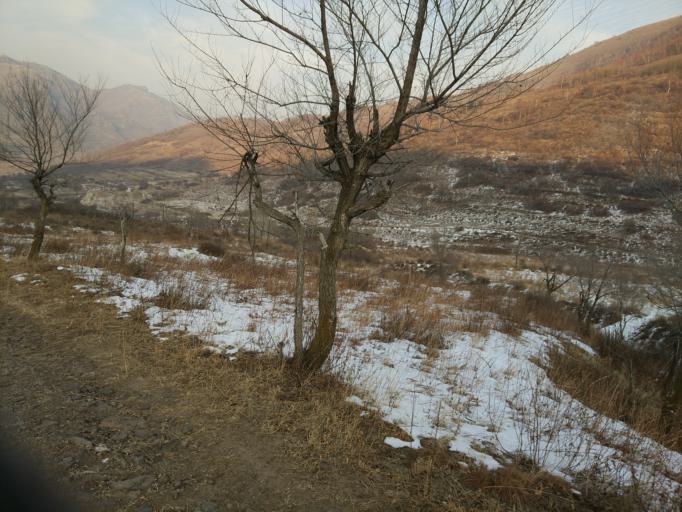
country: CN
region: Hebei
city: Xiwanzi
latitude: 40.8014
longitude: 115.4586
